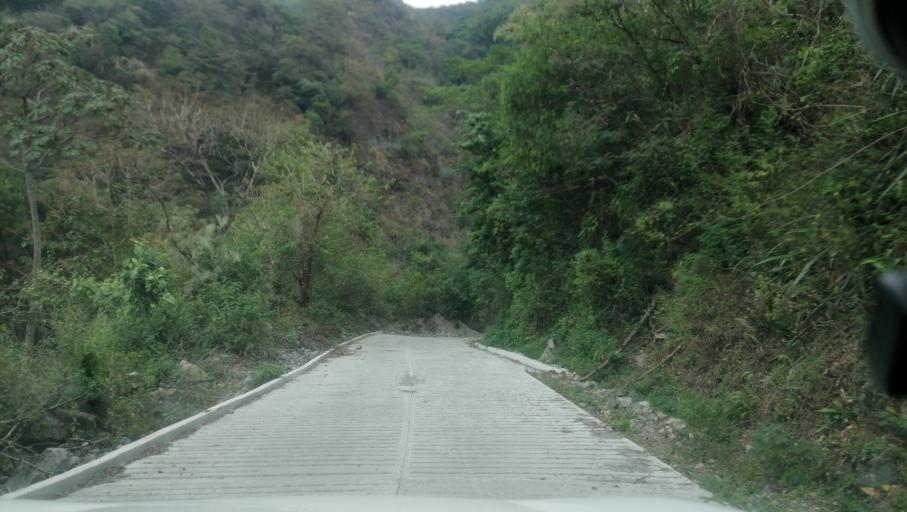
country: MX
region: Chiapas
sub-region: Cacahoatan
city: Benito Juarez
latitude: 15.1658
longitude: -92.1793
